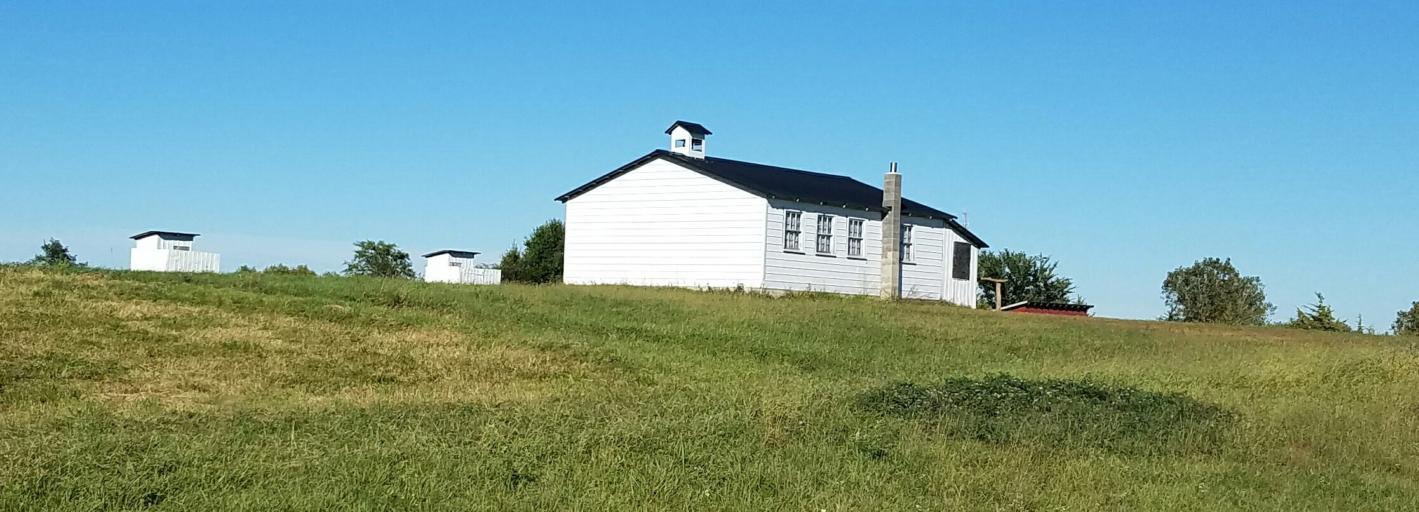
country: US
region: Iowa
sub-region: Decatur County
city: Lamoni
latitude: 40.6381
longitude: -93.8785
